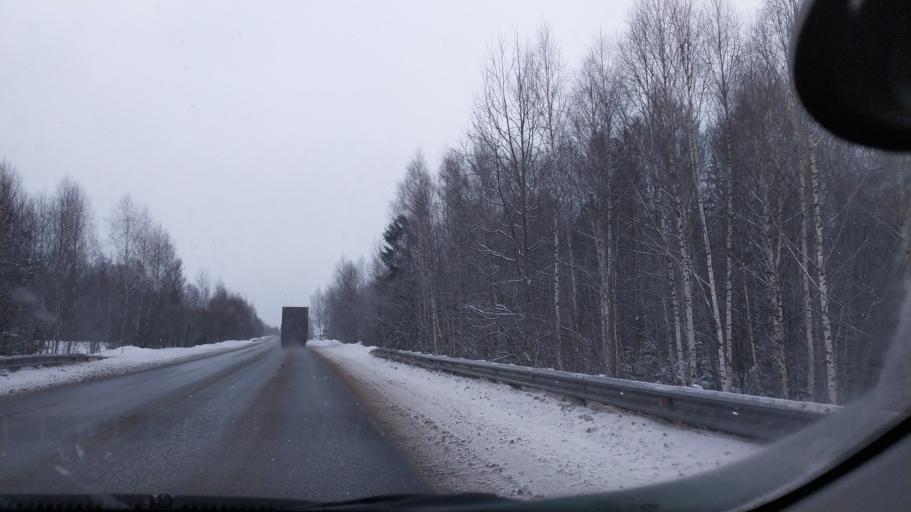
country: RU
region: Mariy-El
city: Krasnogorskiy
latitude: 56.1661
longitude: 48.2346
